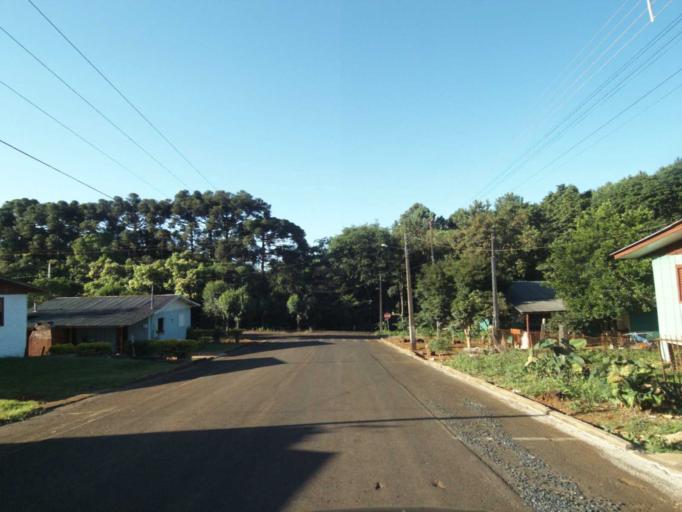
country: BR
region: Parana
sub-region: Coronel Vivida
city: Coronel Vivida
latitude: -25.9573
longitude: -52.8146
